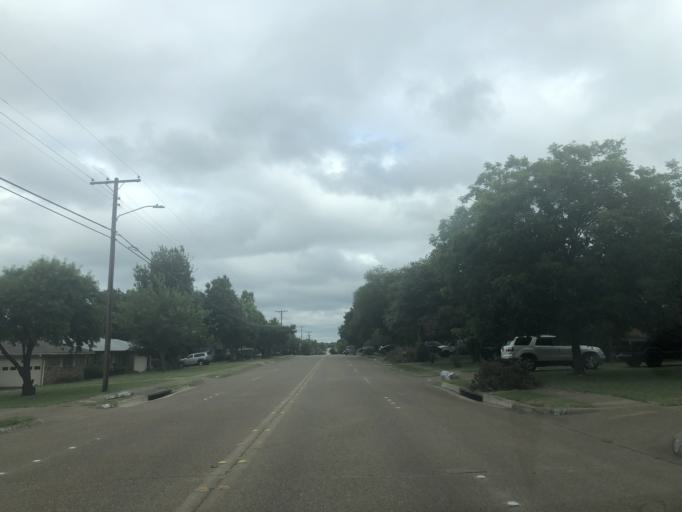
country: US
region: Texas
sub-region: Dallas County
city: Duncanville
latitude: 32.6518
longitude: -96.9137
